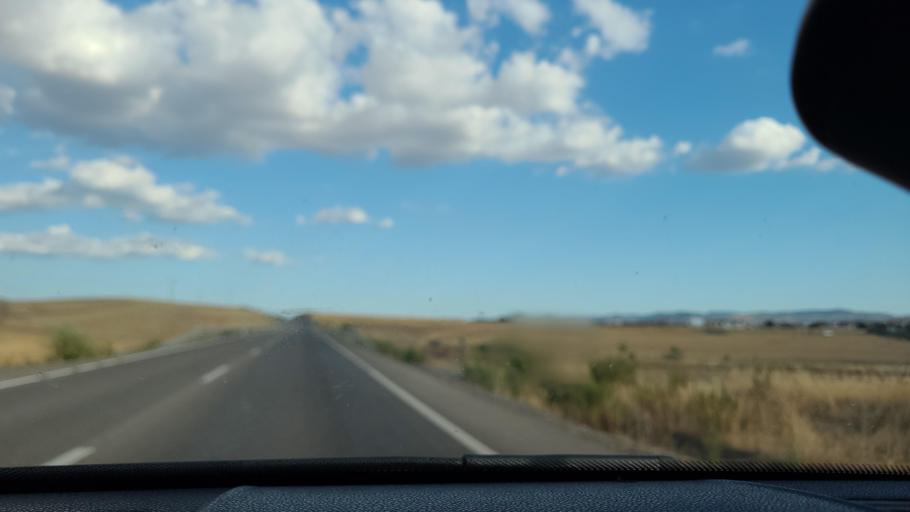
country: ES
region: Andalusia
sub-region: Province of Cordoba
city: Belmez
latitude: 38.2825
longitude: -5.2112
